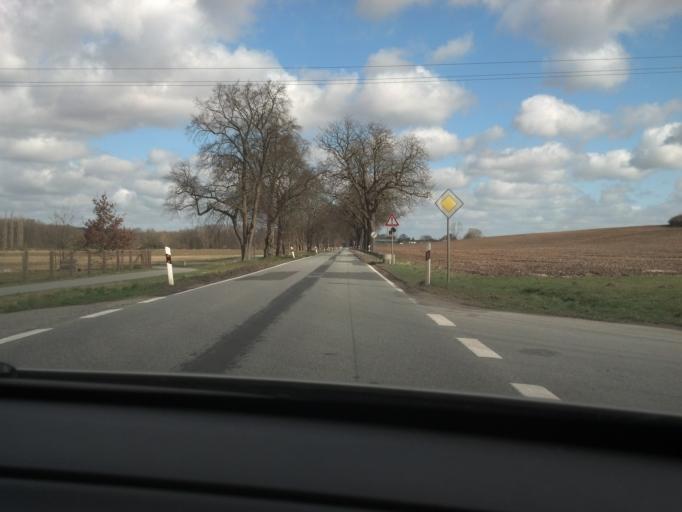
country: DE
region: Mecklenburg-Vorpommern
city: Boizenburg
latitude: 53.4158
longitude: 10.7432
